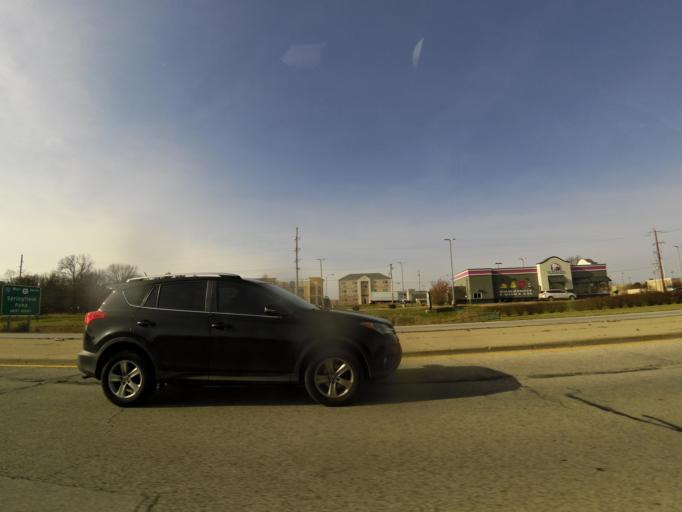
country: US
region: Illinois
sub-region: Macon County
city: Forsyth
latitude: 39.9157
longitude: -88.9553
